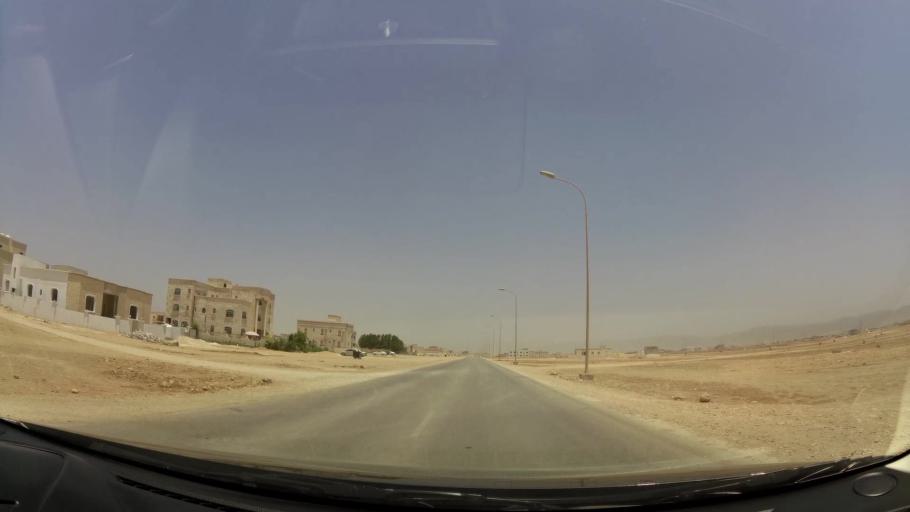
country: OM
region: Zufar
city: Salalah
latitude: 17.0919
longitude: 54.2098
